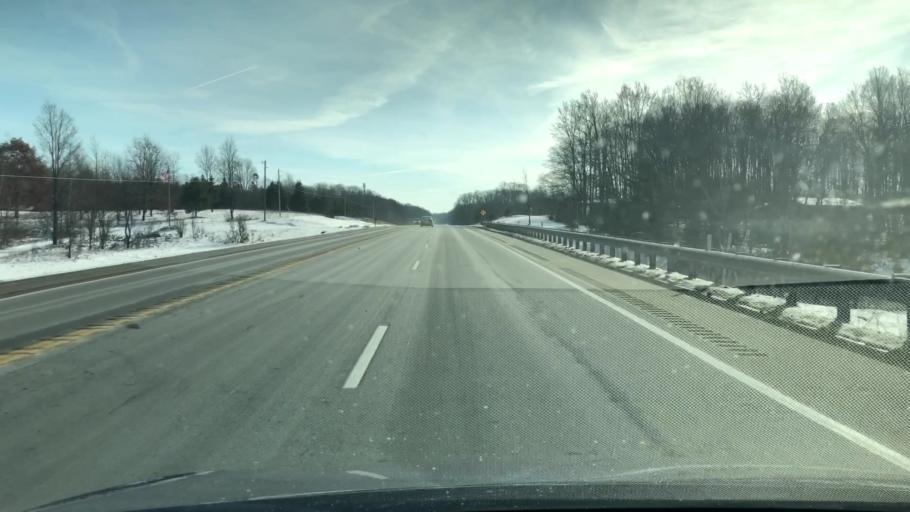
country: US
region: Michigan
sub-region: Kalkaska County
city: Rapid City
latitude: 44.7755
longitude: -85.2814
